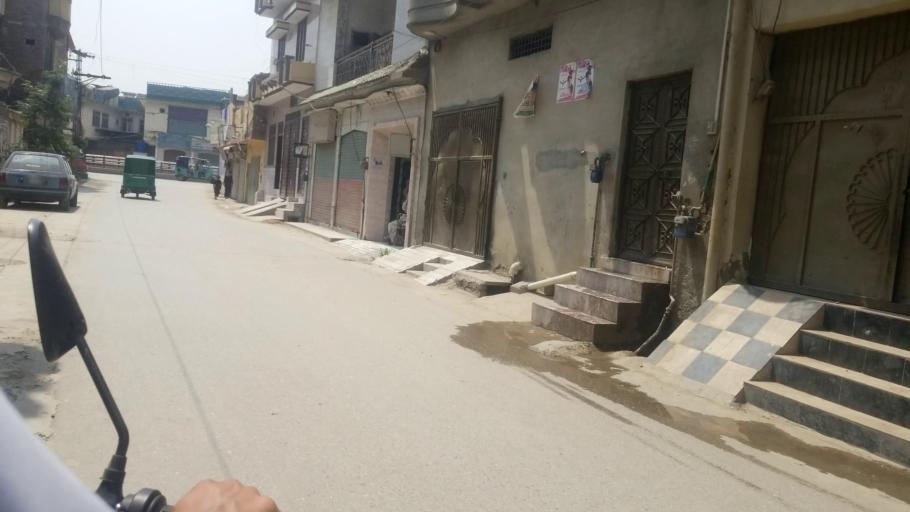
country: PK
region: Khyber Pakhtunkhwa
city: Peshawar
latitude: 34.0255
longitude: 71.5884
